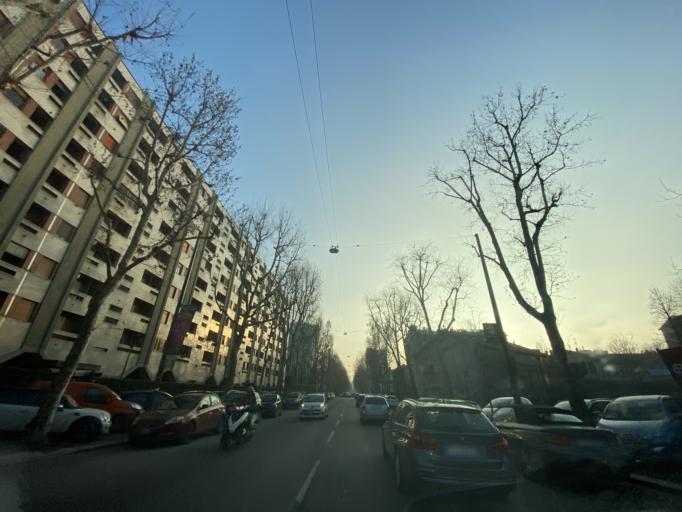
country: IT
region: Lombardy
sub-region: Citta metropolitana di Milano
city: Milano
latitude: 45.4962
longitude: 9.1836
